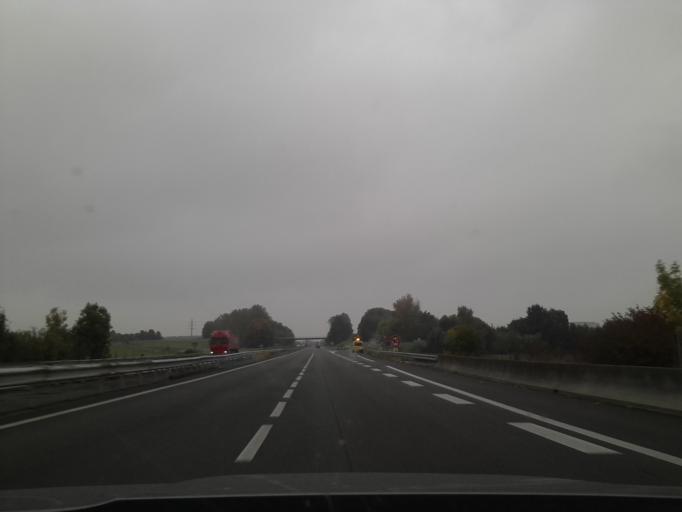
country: FR
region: Nord-Pas-de-Calais
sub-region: Departement du Nord
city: Raillencourt-Sainte-Olle
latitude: 50.1818
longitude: 3.1885
